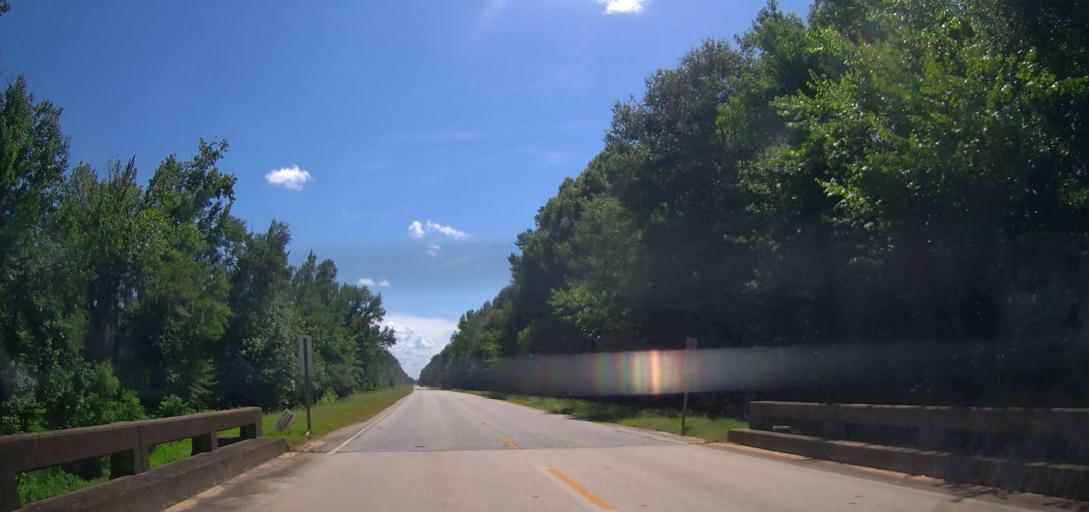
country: US
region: Alabama
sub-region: Elmore County
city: Tallassee
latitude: 32.3928
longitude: -85.9759
